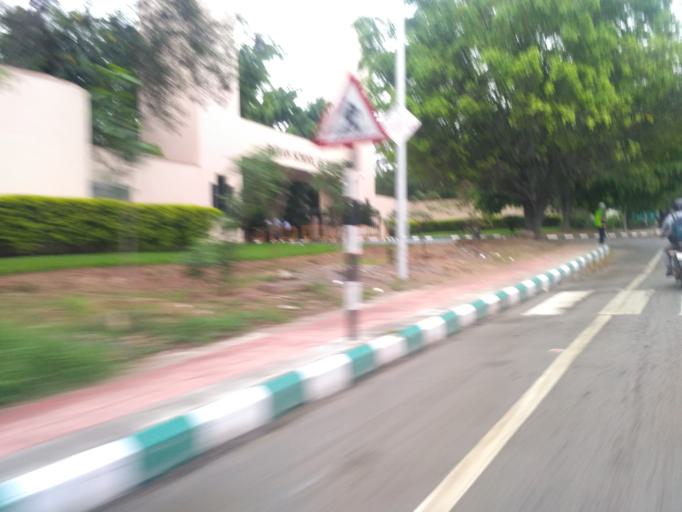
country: IN
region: Telangana
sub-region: Medak
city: Serilingampalle
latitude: 17.4357
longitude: 78.3466
